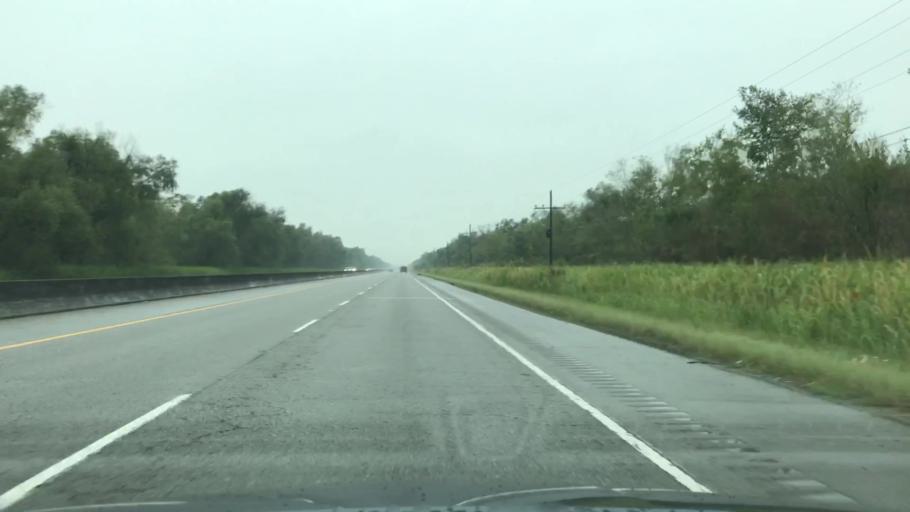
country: US
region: Louisiana
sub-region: Saint Charles Parish
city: Des Allemands
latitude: 29.7795
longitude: -90.5274
